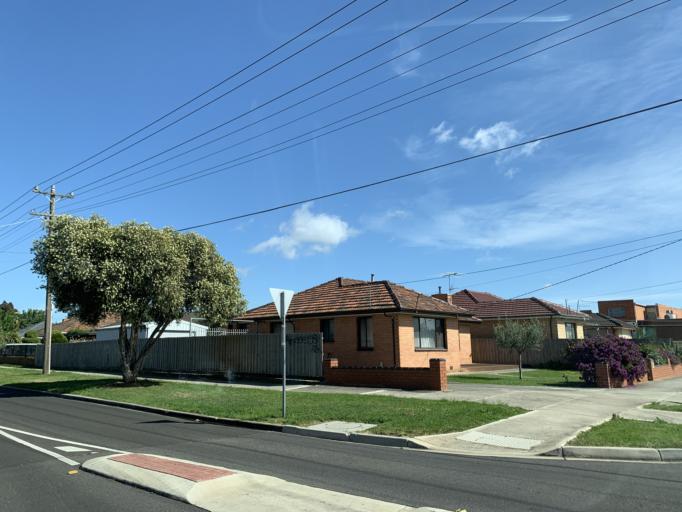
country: AU
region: Victoria
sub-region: Brimbank
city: Saint Albans
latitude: -37.7357
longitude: 144.8059
